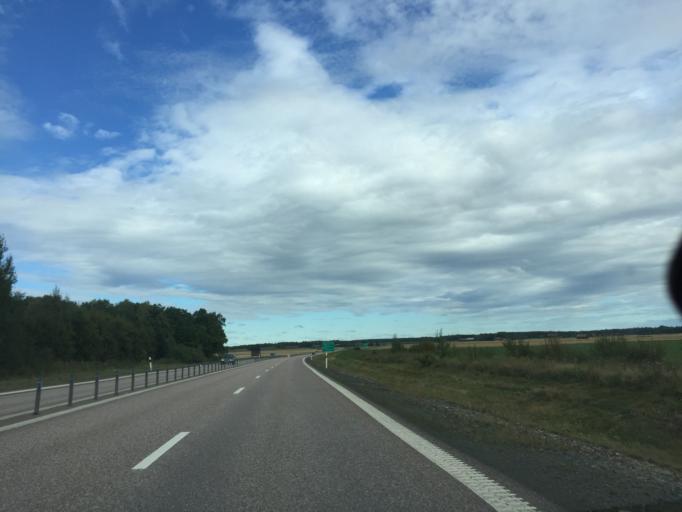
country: SE
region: Vaestmanland
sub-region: Arboga Kommun
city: Arboga
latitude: 59.4178
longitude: 15.8857
